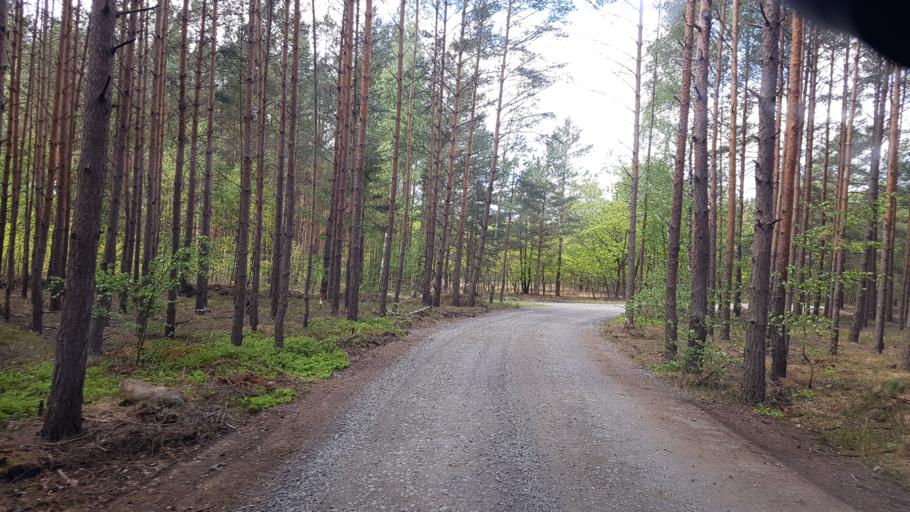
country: DE
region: Brandenburg
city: Altdobern
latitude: 51.6380
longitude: 13.9769
